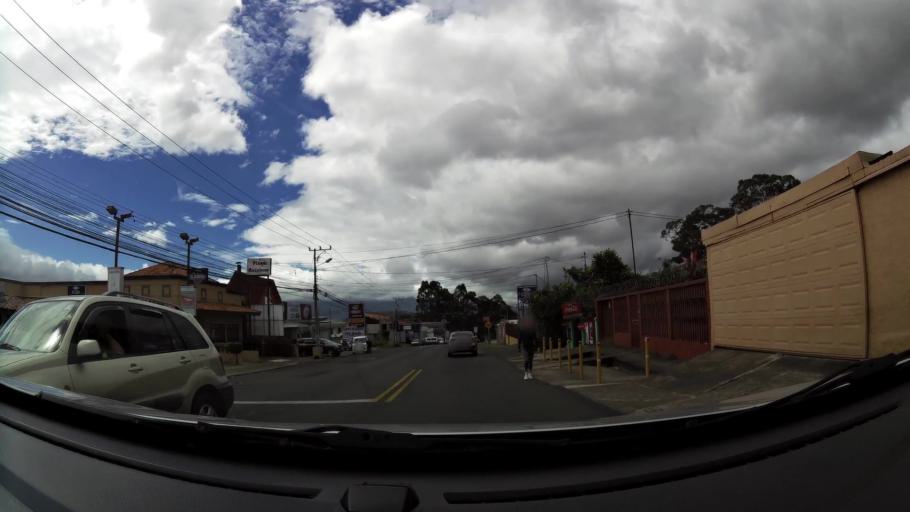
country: CR
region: Cartago
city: San Diego
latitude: 9.9086
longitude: -84.0072
